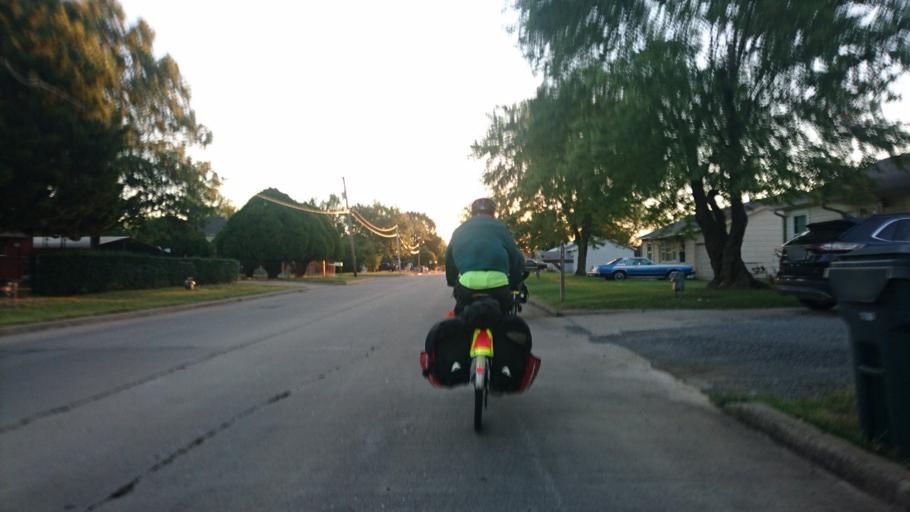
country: US
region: Oklahoma
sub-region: Rogers County
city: Claremore
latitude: 36.3111
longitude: -95.6277
